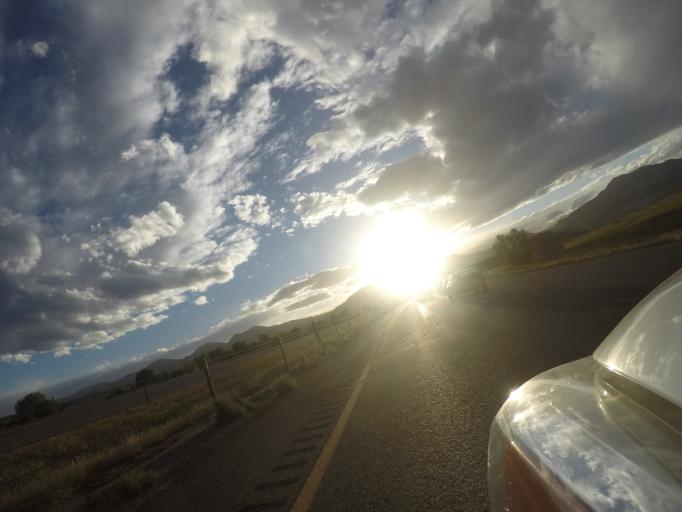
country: US
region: Colorado
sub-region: Jefferson County
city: Ken Caryl
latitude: 39.6394
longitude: -105.1396
